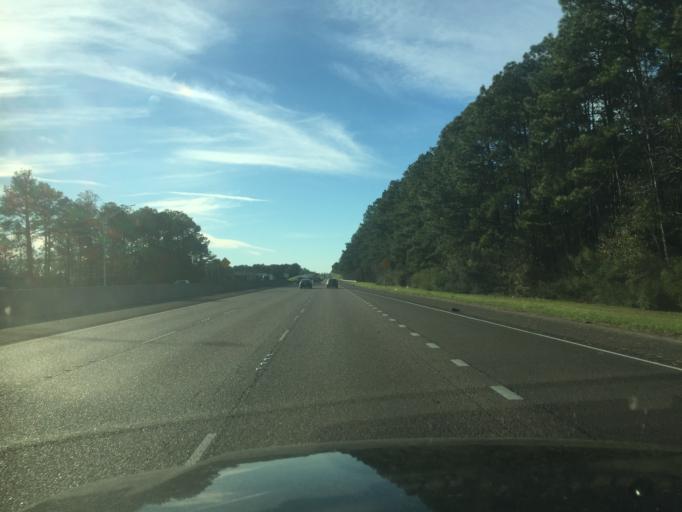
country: US
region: Louisiana
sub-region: Saint Tammany Parish
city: Slidell
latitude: 30.3104
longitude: -89.7770
